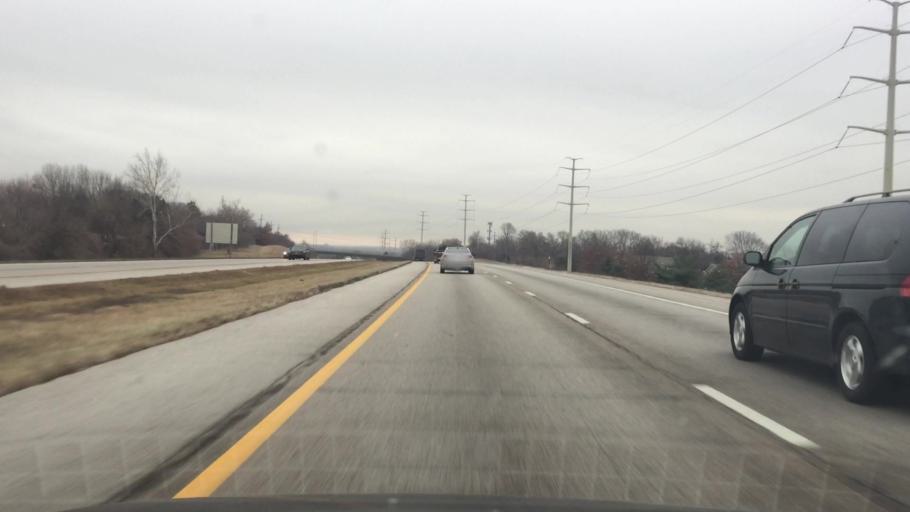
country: US
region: Kansas
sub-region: Johnson County
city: Lenexa
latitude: 38.9079
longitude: -94.6921
